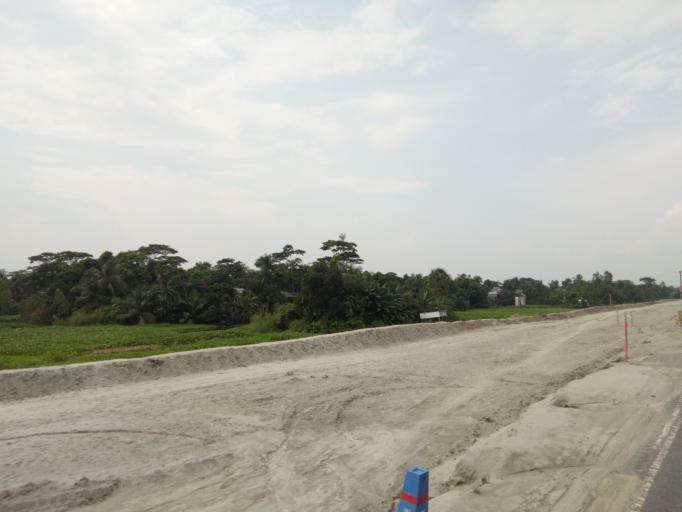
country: BD
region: Dhaka
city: Dohar
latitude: 23.5762
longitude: 90.3048
